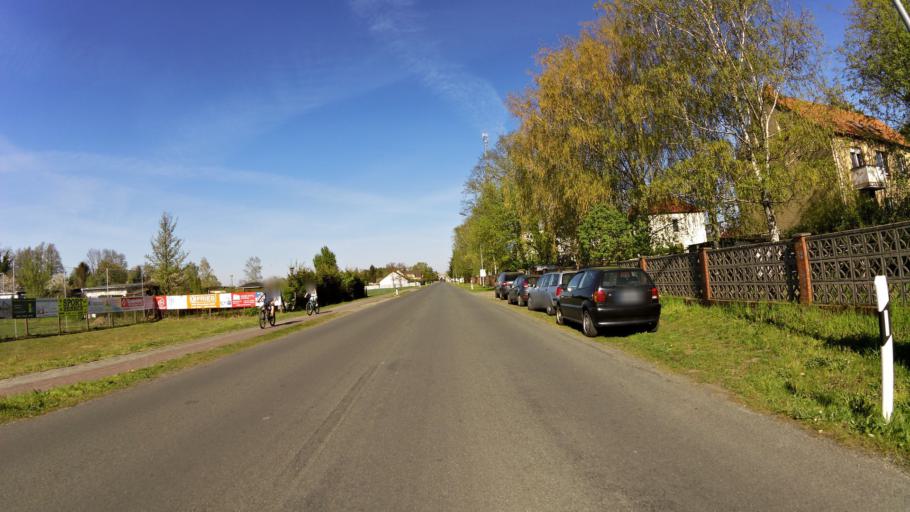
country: DE
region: Saxony-Anhalt
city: Stendal
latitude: 52.5848
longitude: 11.8292
